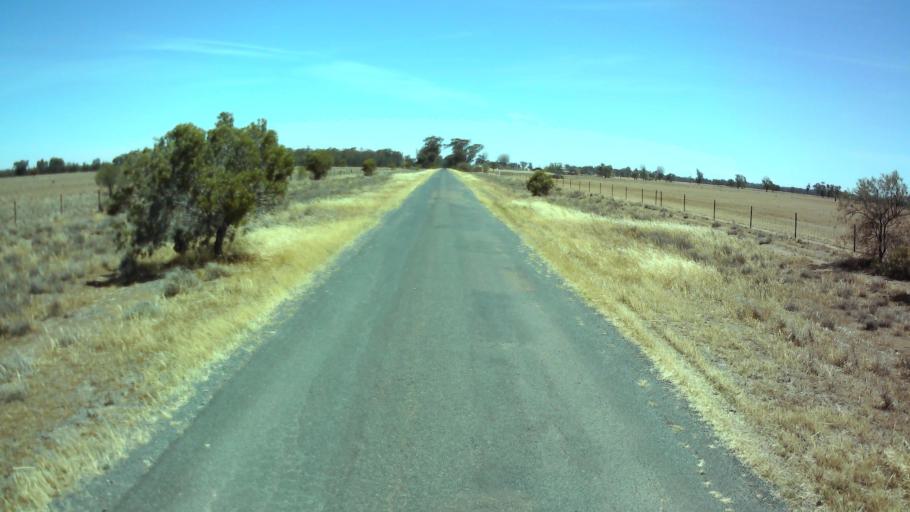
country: AU
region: New South Wales
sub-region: Weddin
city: Grenfell
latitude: -33.8966
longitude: 147.6872
